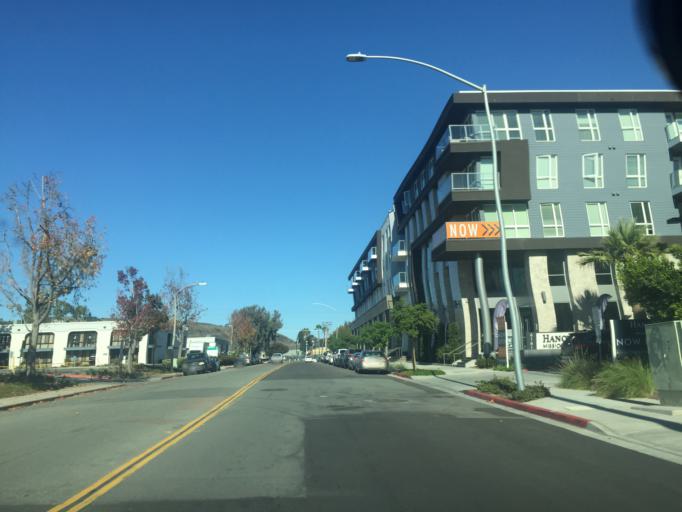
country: US
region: California
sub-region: San Diego County
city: La Mesa
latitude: 32.7857
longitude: -117.1015
